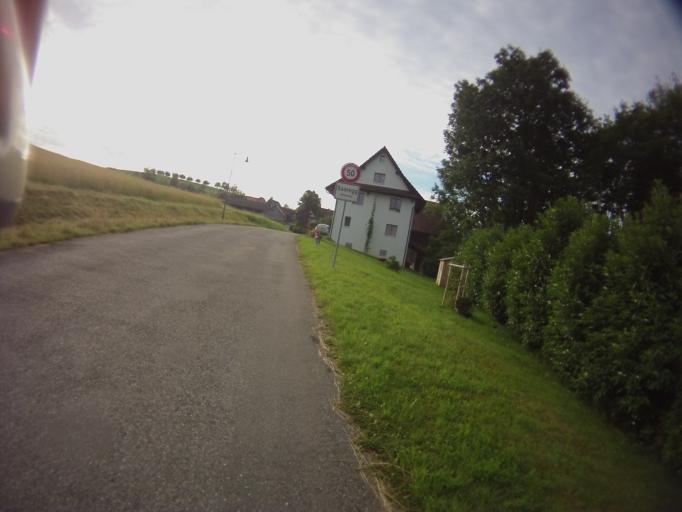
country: CH
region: Zurich
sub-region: Bezirk Affoltern
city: Knonau
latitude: 47.2167
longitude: 8.4738
